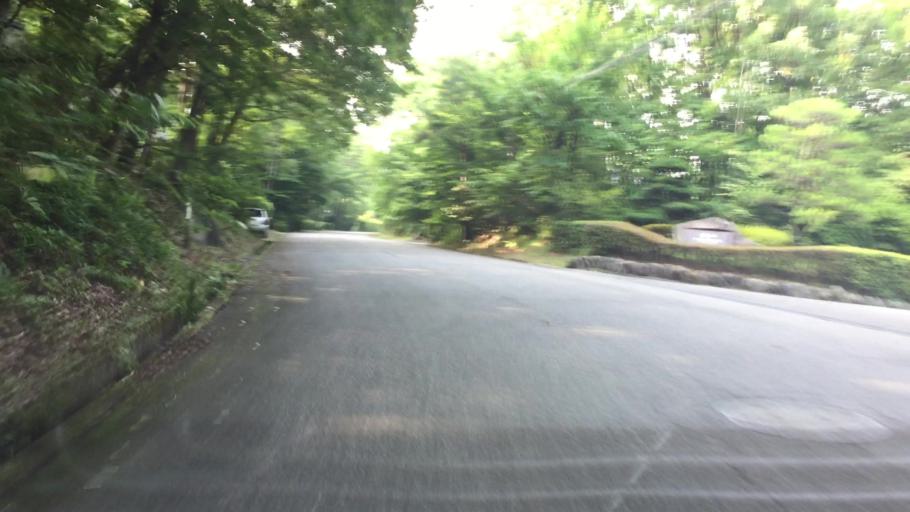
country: JP
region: Tochigi
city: Kuroiso
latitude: 37.0989
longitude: 140.0437
